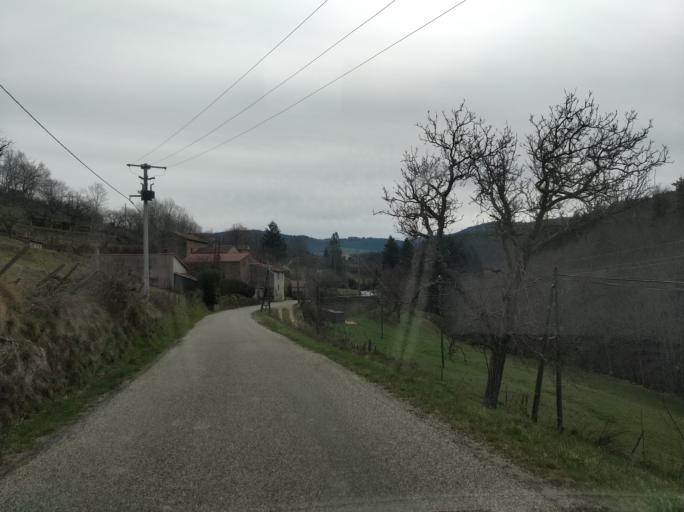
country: FR
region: Rhone-Alpes
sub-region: Departement de l'Ardeche
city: Satillieu
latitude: 45.1581
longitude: 4.5939
